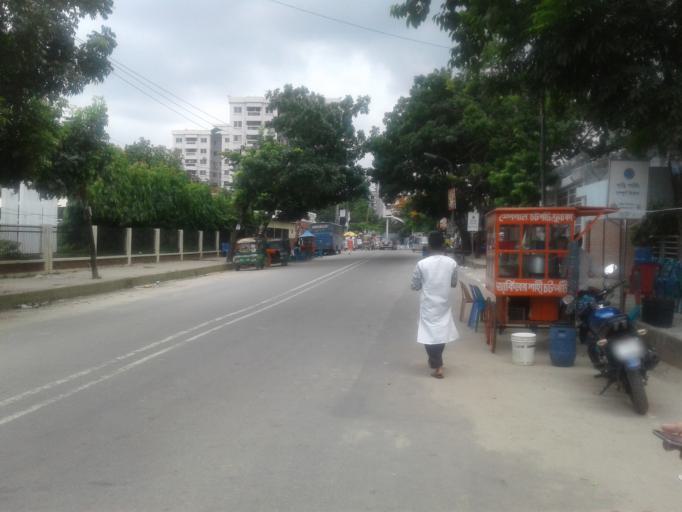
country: BD
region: Dhaka
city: Azimpur
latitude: 23.8057
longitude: 90.3770
